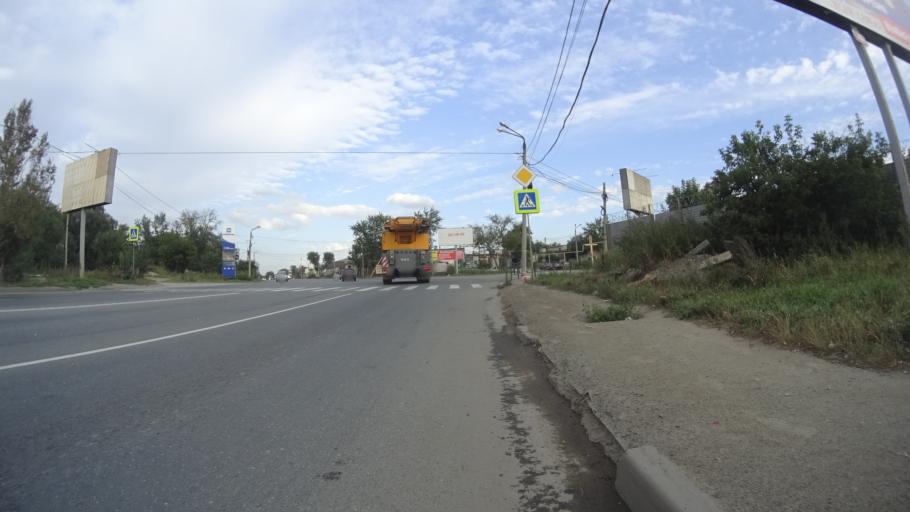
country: RU
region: Chelyabinsk
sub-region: Gorod Chelyabinsk
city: Chelyabinsk
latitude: 55.1921
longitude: 61.4232
